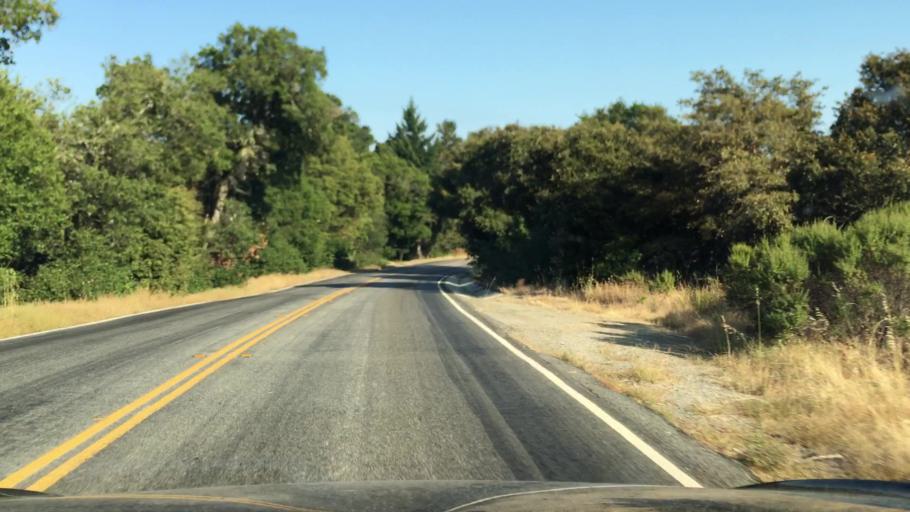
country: US
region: California
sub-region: San Mateo County
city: Portola Valley
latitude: 37.3180
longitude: -122.1906
